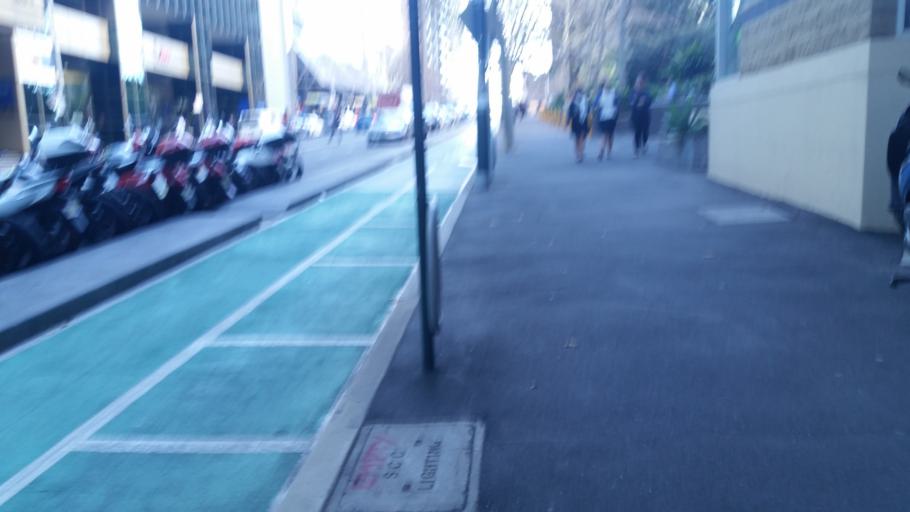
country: AU
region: New South Wales
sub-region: City of Sydney
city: Sydney
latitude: -33.8643
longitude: 151.2039
